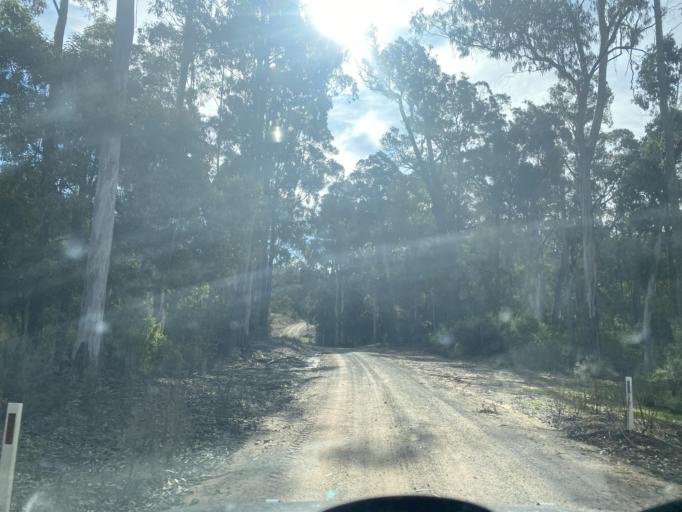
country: AU
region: Victoria
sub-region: Mansfield
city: Mansfield
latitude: -36.8806
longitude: 146.1911
